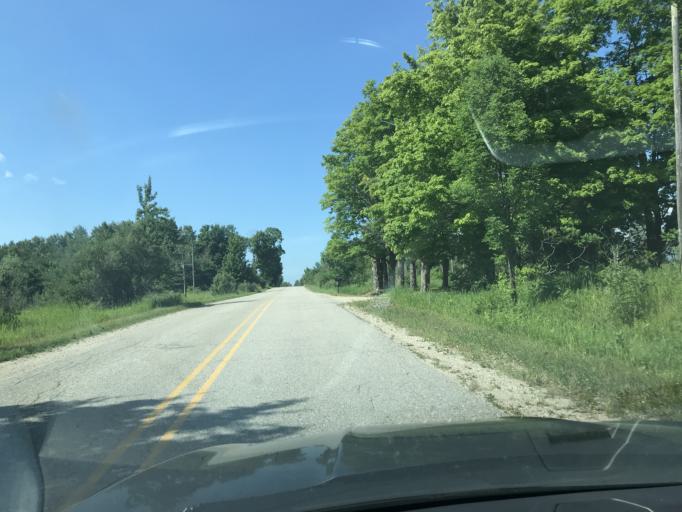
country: US
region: Michigan
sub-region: Cheboygan County
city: Cheboygan
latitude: 45.6201
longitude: -84.6714
